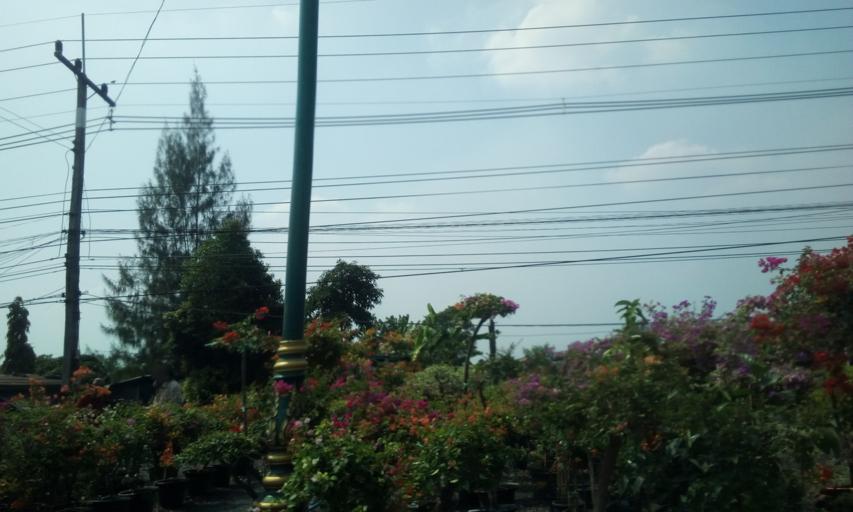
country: TH
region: Nakhon Nayok
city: Ongkharak
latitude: 14.1155
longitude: 100.9433
